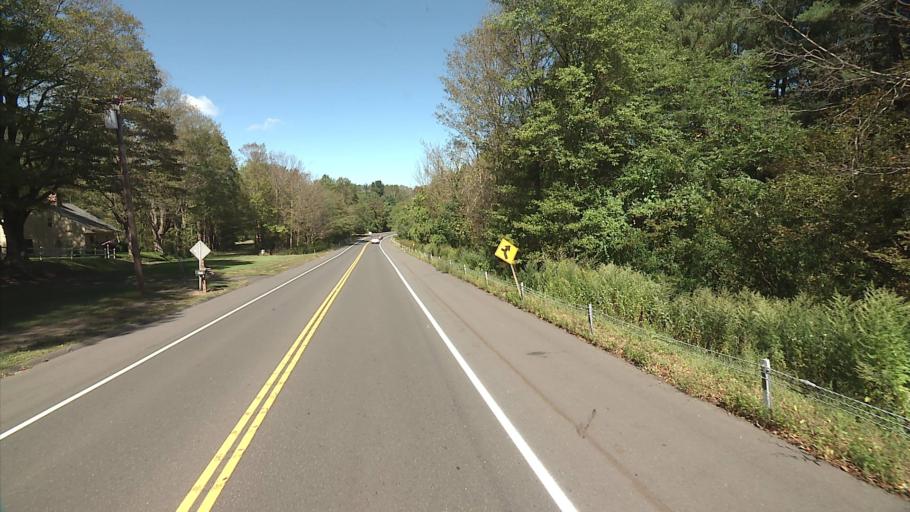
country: US
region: Connecticut
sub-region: New Haven County
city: Prospect
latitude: 41.4269
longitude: -72.9753
